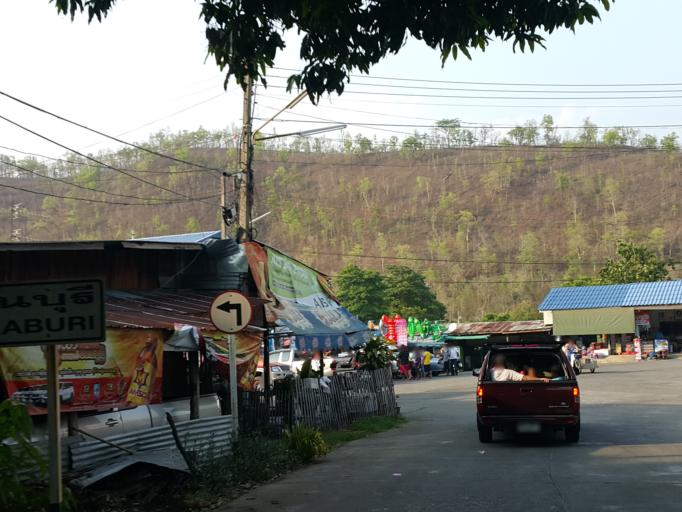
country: TH
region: Kanchanaburi
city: Si Sawat
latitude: 14.3829
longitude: 99.1362
